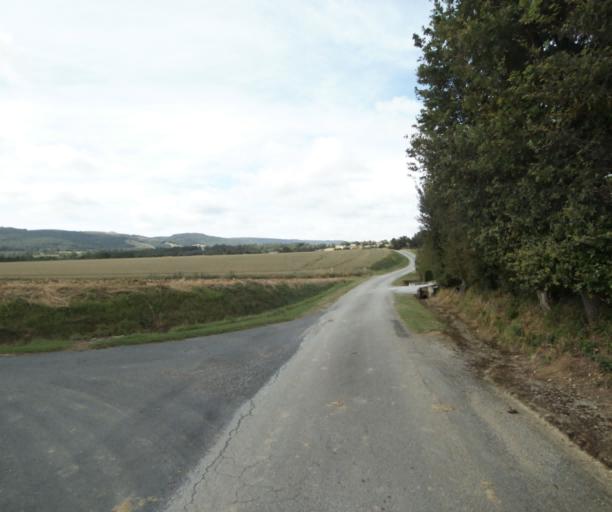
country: FR
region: Midi-Pyrenees
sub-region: Departement du Tarn
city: Soreze
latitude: 43.4775
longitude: 2.0877
